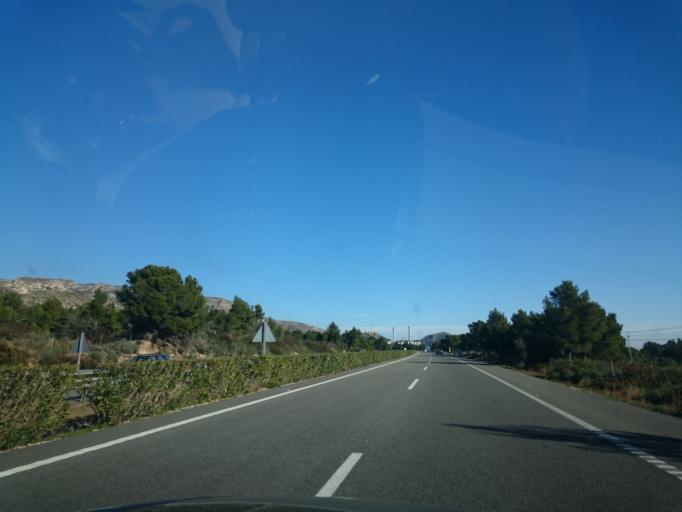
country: ES
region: Catalonia
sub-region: Provincia de Tarragona
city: l'Ametlla de Mar
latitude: 40.9437
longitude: 0.8549
